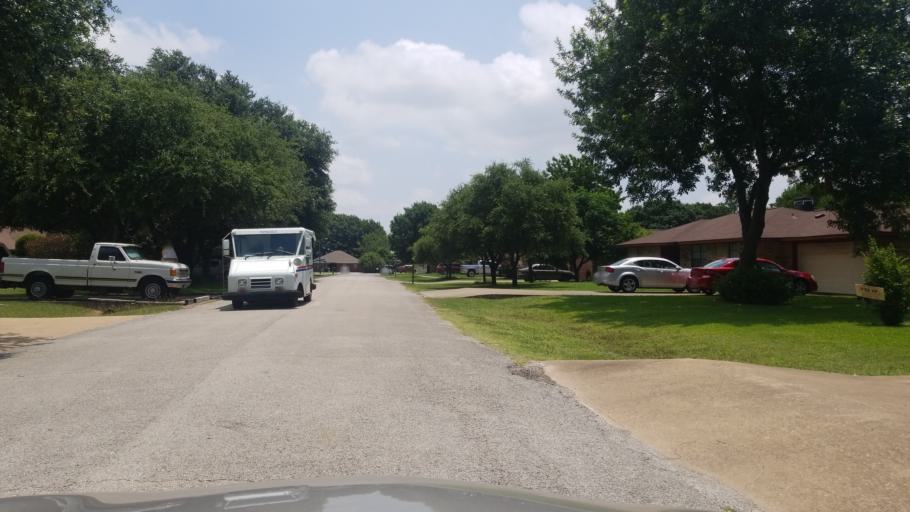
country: US
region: Texas
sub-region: Dallas County
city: Duncanville
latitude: 32.6737
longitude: -96.9114
